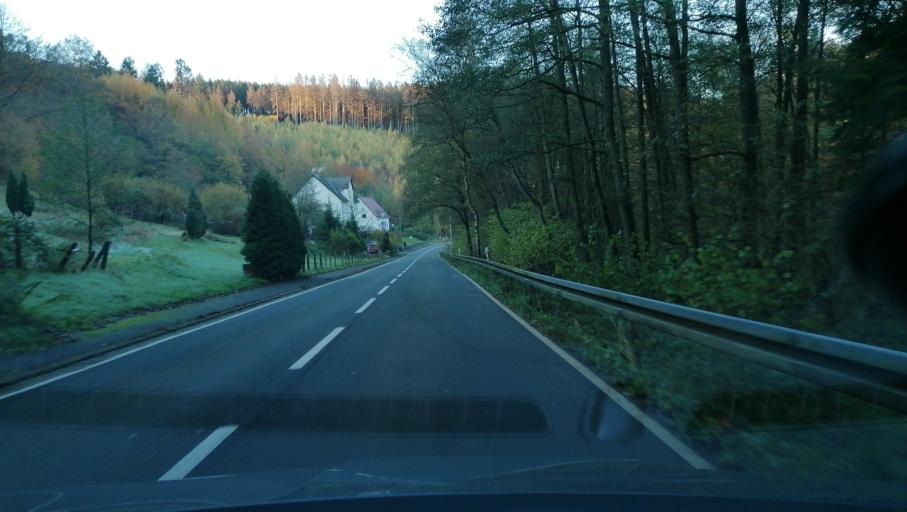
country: DE
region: North Rhine-Westphalia
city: Ennepetal
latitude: 51.2795
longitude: 7.3353
